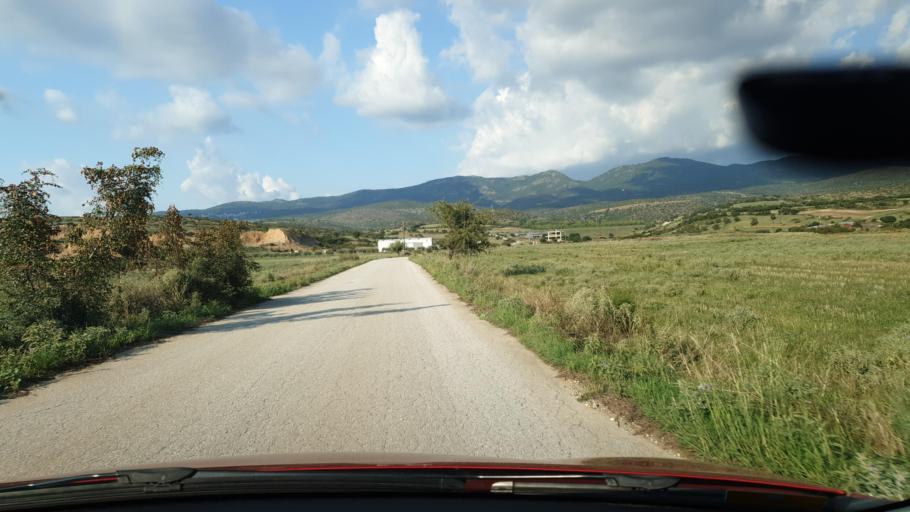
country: GR
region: Central Macedonia
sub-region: Nomos Thessalonikis
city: Vasilika
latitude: 40.4986
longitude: 23.1426
